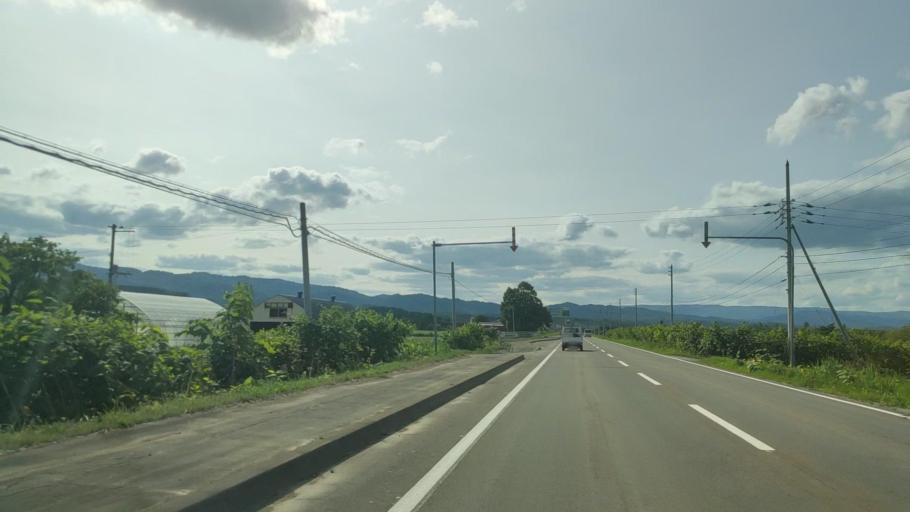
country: JP
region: Hokkaido
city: Nayoro
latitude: 44.4429
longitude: 142.3773
